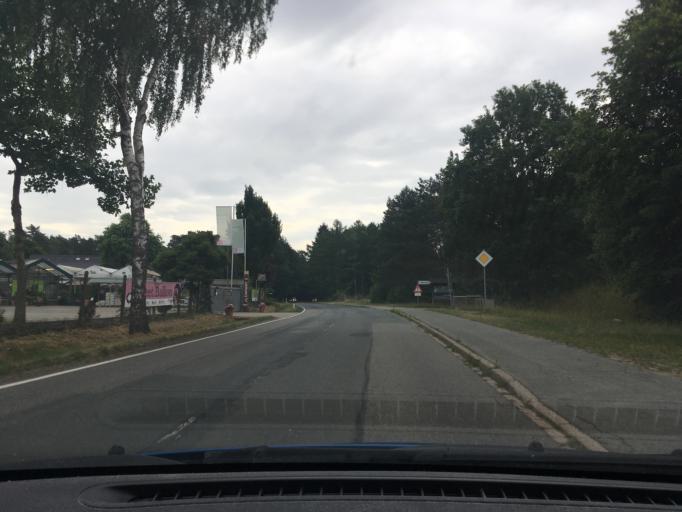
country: DE
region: Lower Saxony
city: Hollenstedt
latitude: 53.3608
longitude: 9.7257
